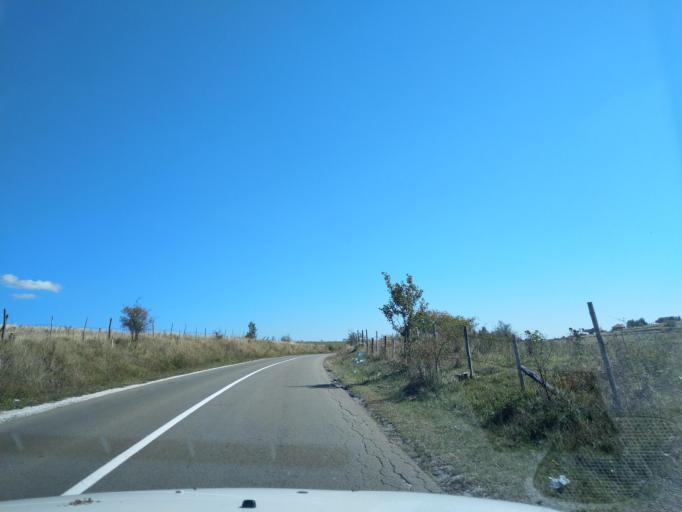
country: RS
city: Sokolovica
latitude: 43.2767
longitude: 20.2195
